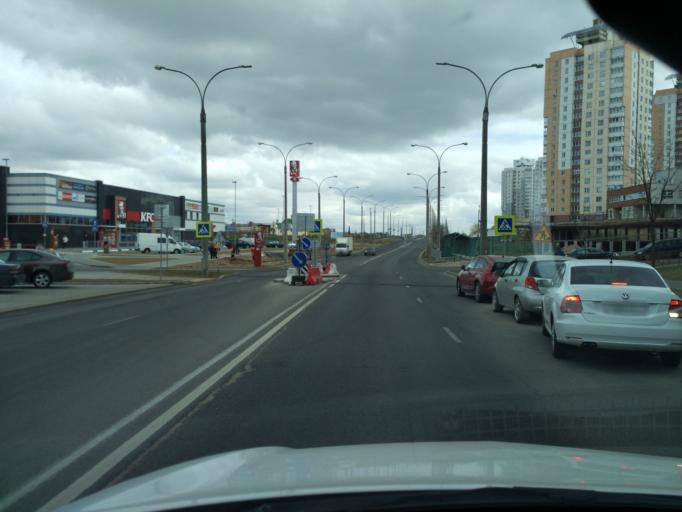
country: BY
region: Minsk
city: Shchomyslitsa
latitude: 53.8494
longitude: 27.4840
